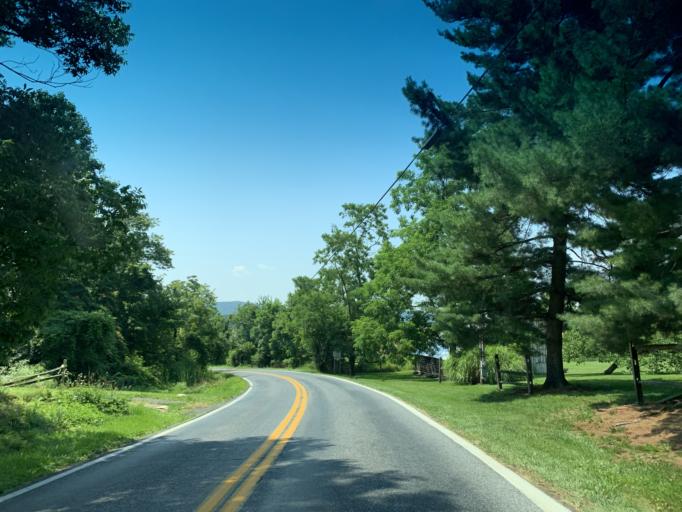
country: US
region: Maryland
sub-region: Montgomery County
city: Clarksburg
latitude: 39.2473
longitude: -77.3504
